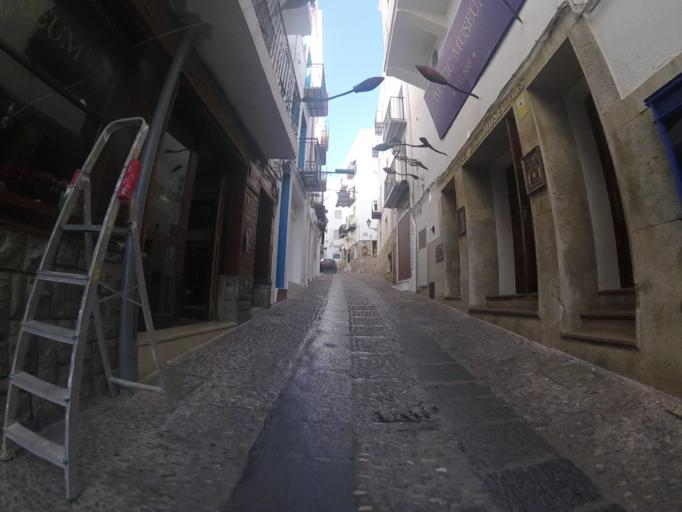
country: ES
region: Valencia
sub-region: Provincia de Castello
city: Peniscola
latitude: 40.3575
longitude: 0.4077
